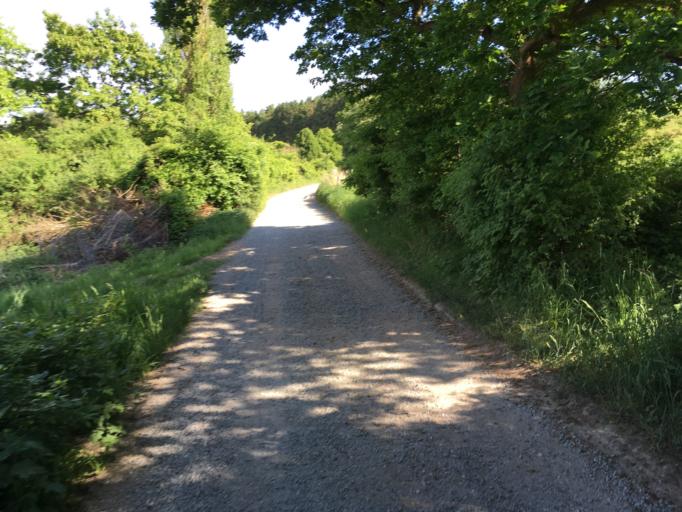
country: DK
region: Capital Region
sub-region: Ballerup Kommune
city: Ballerup
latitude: 55.7516
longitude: 12.3575
